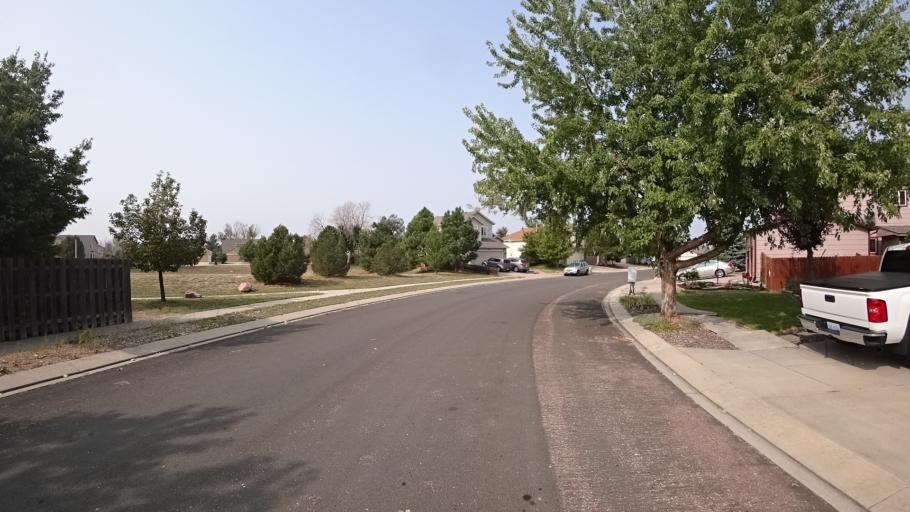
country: US
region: Colorado
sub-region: El Paso County
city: Cimarron Hills
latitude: 38.9249
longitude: -104.7244
